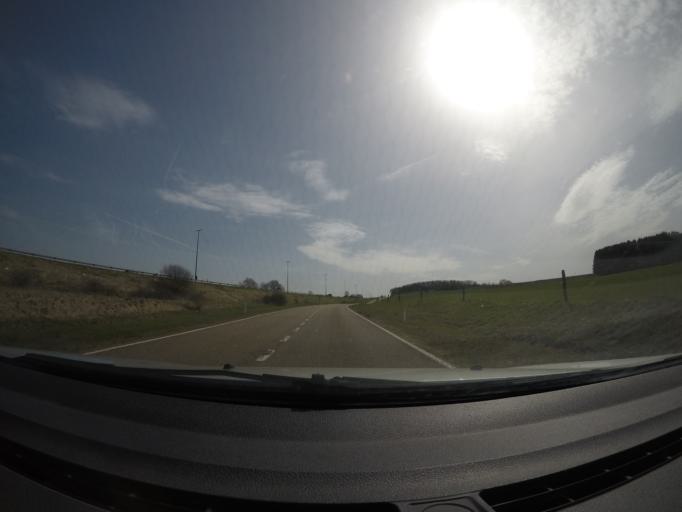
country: BE
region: Wallonia
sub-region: Province du Luxembourg
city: Habay-la-Vieille
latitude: 49.7187
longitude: 5.5932
